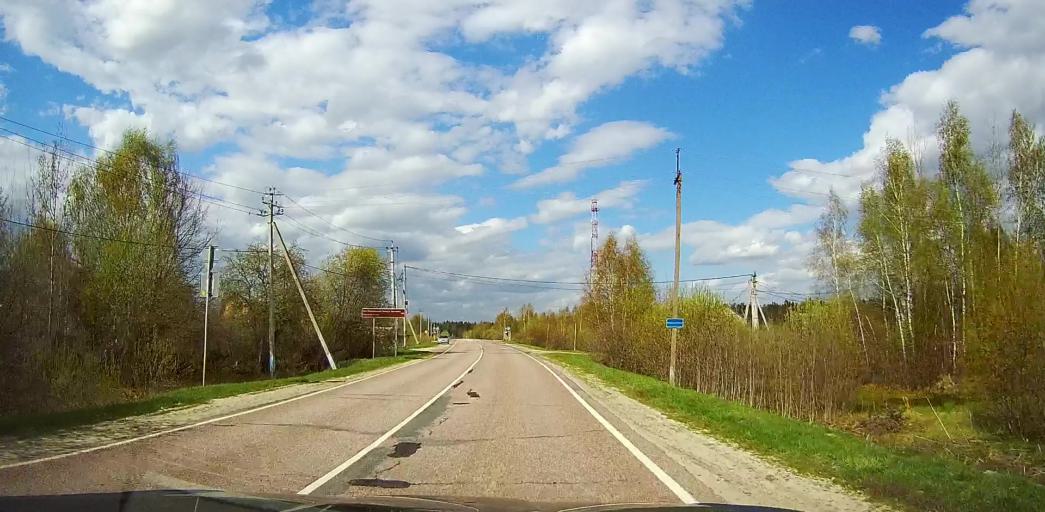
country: RU
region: Moskovskaya
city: Rakhmanovo
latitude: 55.6540
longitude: 38.6393
